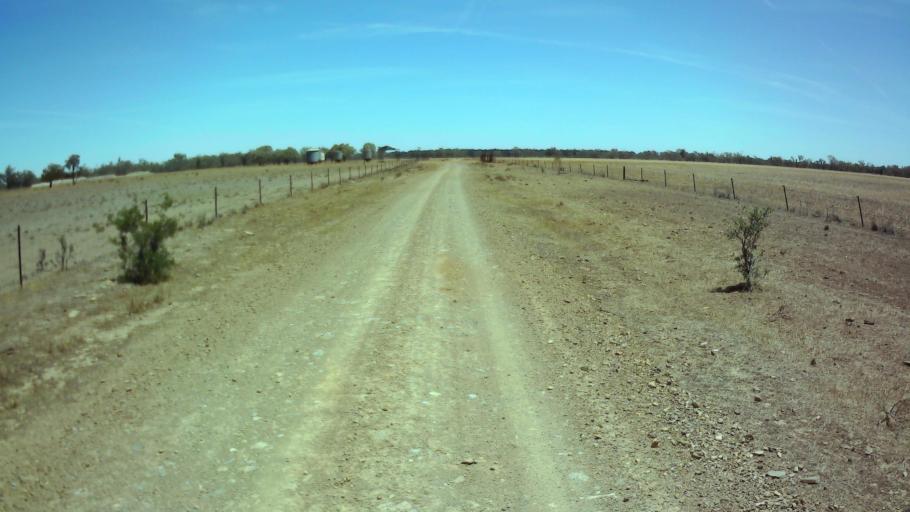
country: AU
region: New South Wales
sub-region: Bland
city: West Wyalong
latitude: -33.8260
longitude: 147.6399
